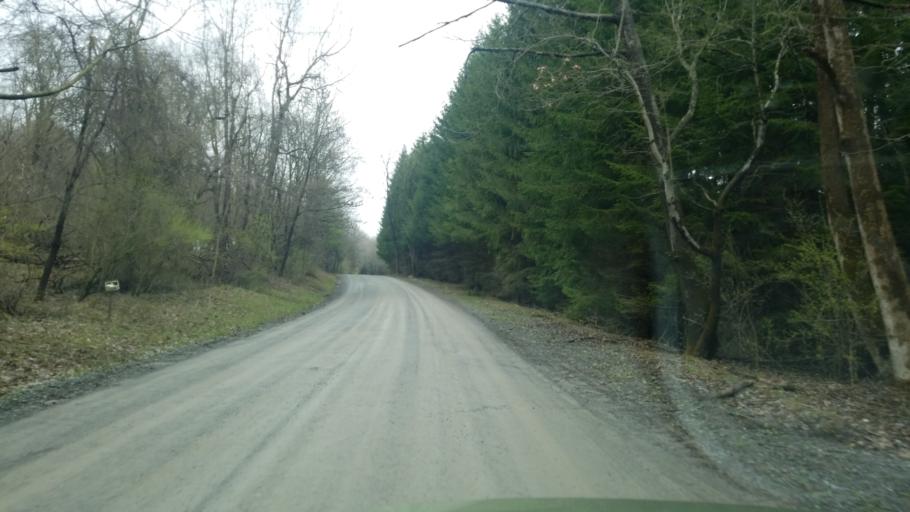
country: US
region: Pennsylvania
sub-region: Clearfield County
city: Shiloh
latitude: 41.1291
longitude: -78.3342
